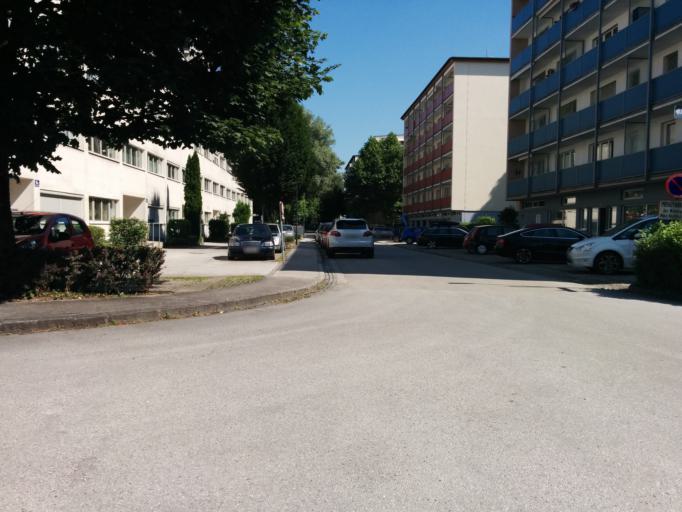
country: AT
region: Salzburg
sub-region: Salzburg Stadt
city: Salzburg
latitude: 47.7878
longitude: 13.0640
